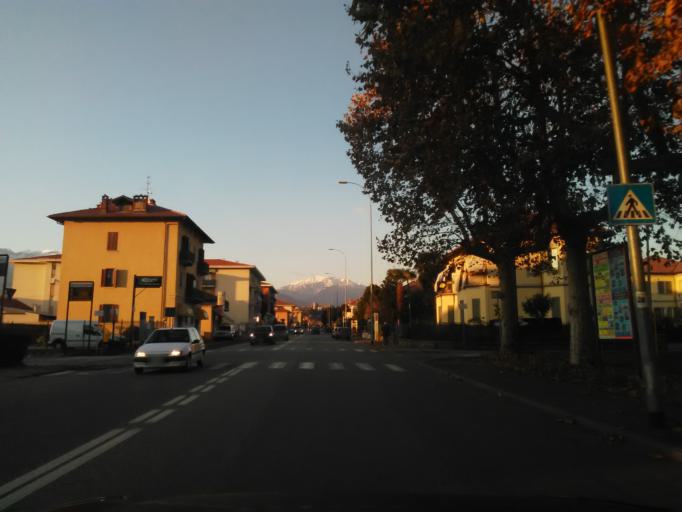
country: IT
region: Piedmont
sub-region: Provincia di Biella
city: Ponderano
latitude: 45.5469
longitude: 8.0518
